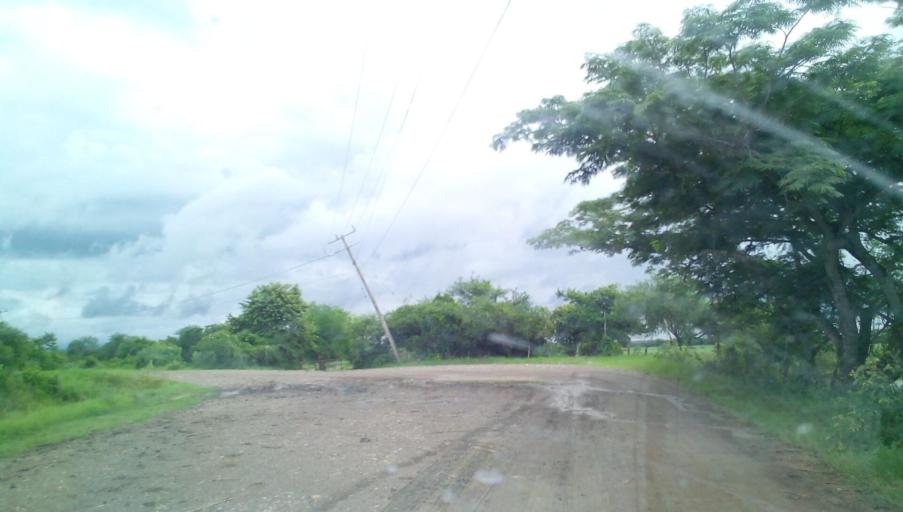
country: MX
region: Veracruz
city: Panuco
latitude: 21.8441
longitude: -98.1307
